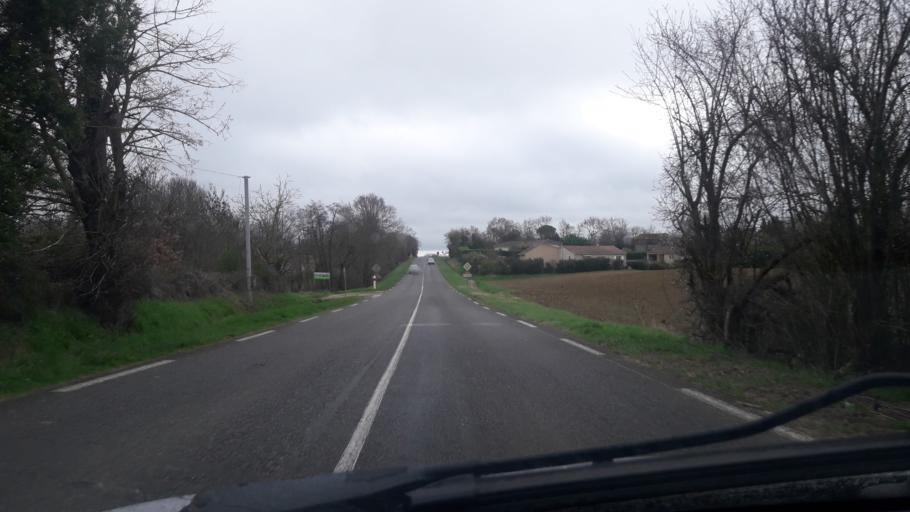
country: FR
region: Midi-Pyrenees
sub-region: Departement du Gers
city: Gimont
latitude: 43.7030
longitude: 0.9949
